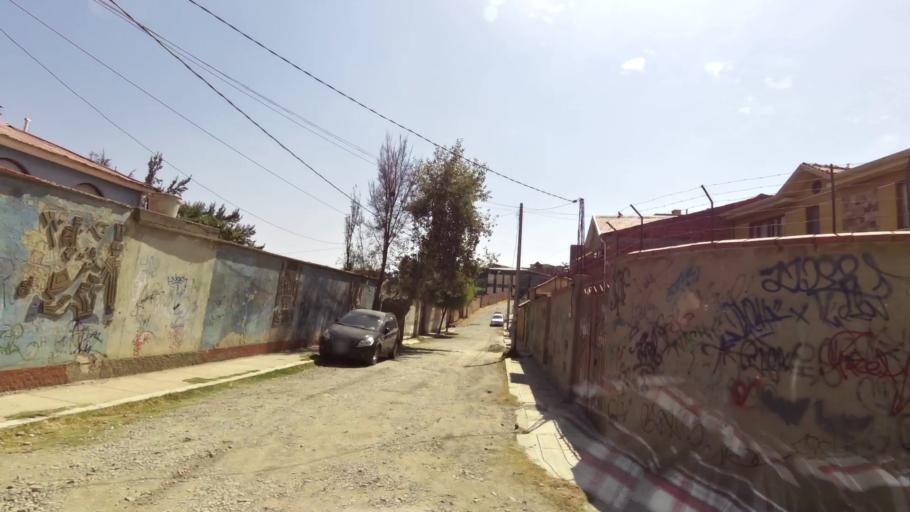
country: BO
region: La Paz
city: La Paz
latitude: -16.5394
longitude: -68.0464
